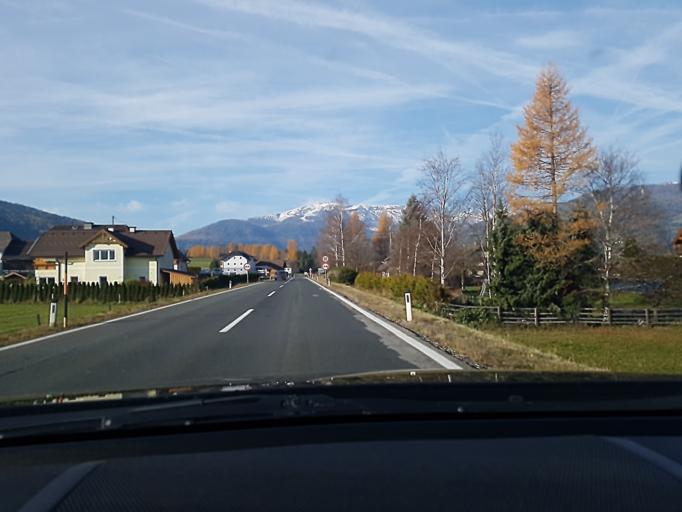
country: AT
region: Salzburg
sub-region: Politischer Bezirk Tamsweg
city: Mariapfarr
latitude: 47.1409
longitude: 13.7467
